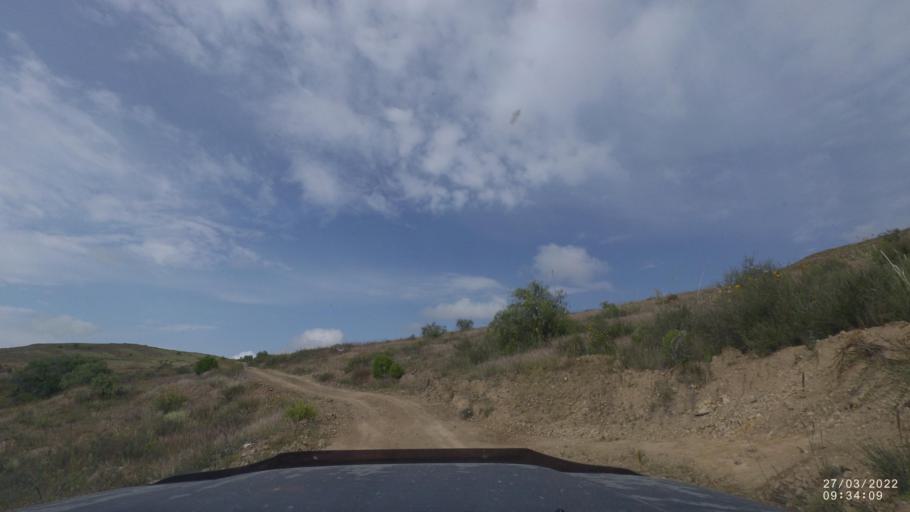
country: BO
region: Cochabamba
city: Cliza
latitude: -17.7415
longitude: -65.8910
